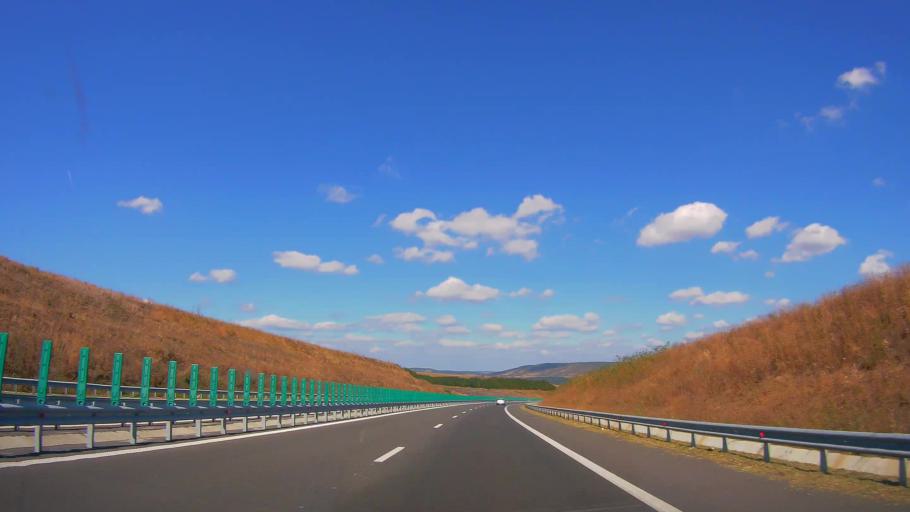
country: RO
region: Cluj
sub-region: Comuna Baciu
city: Mera
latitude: 46.7883
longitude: 23.4162
